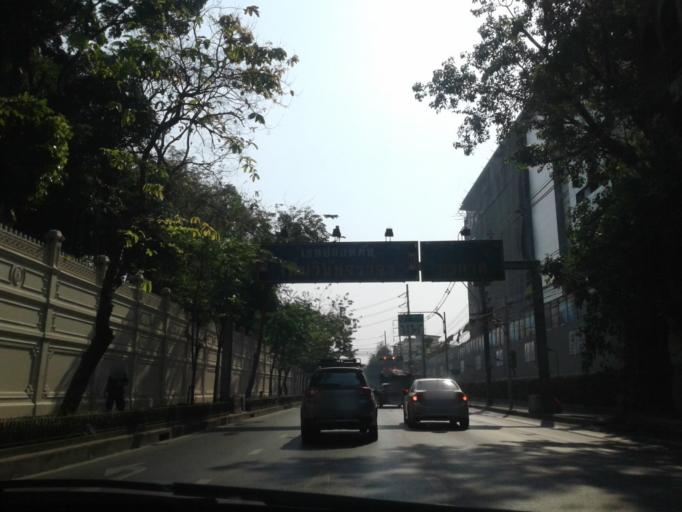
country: TH
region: Bangkok
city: Dusit
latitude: 13.7818
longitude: 100.5088
